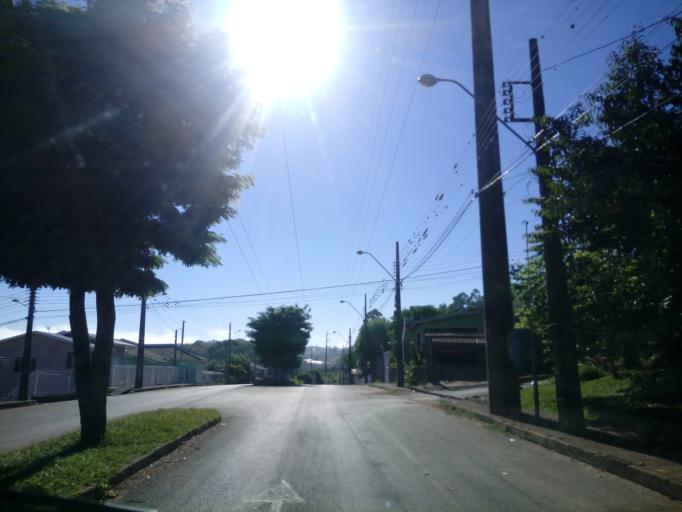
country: BR
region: Santa Catarina
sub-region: Chapeco
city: Chapeco
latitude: -27.0658
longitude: -52.6040
